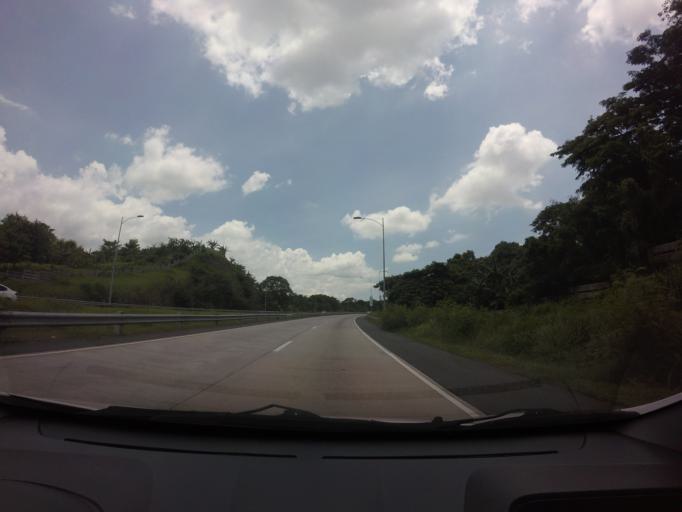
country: PH
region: Calabarzon
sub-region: Province of Laguna
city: San Pedro
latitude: 14.3774
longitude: 121.0291
